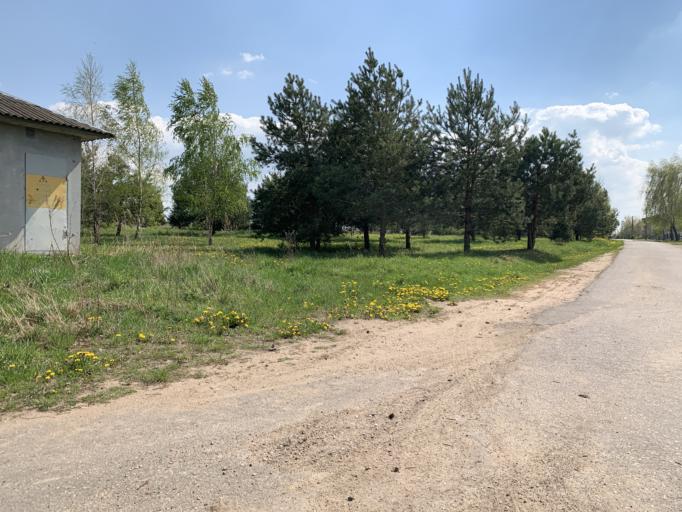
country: BY
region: Minsk
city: Nyasvizh
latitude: 53.2388
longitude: 26.6863
